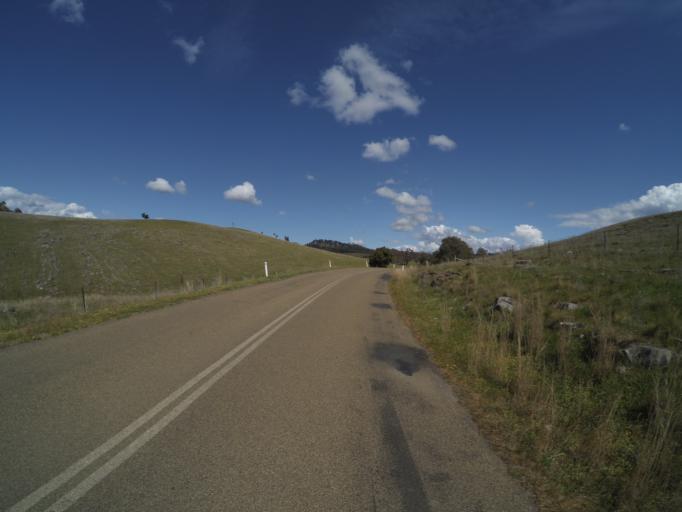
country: AU
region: New South Wales
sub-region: Yass Valley
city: Murrumbateman
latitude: -35.0166
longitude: 148.8535
